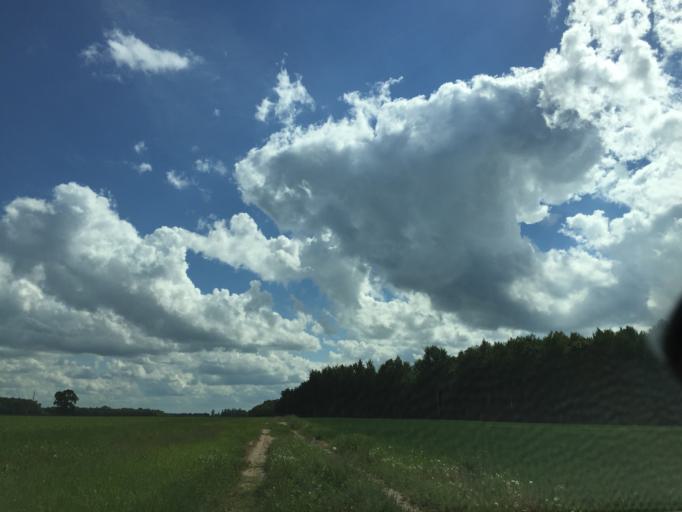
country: LV
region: Dobeles Rajons
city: Dobele
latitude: 56.6843
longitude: 23.4004
